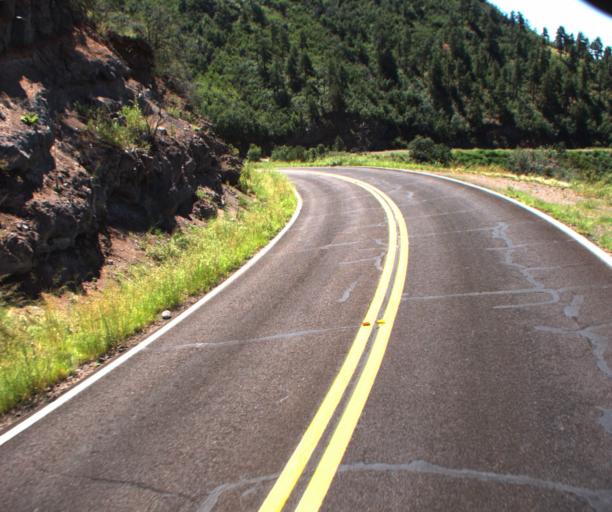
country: US
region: Arizona
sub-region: Greenlee County
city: Morenci
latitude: 33.4395
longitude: -109.3756
